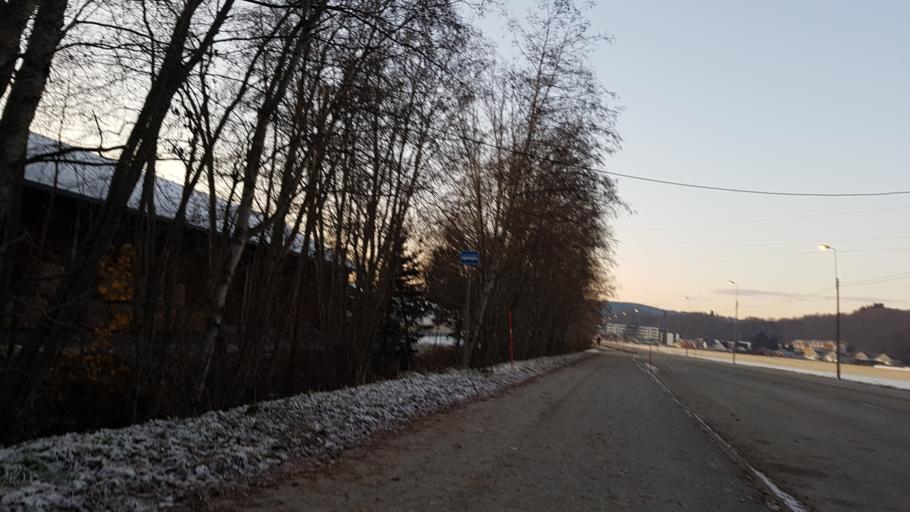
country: NO
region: Sor-Trondelag
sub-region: Melhus
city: Melhus
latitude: 63.2782
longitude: 10.2906
